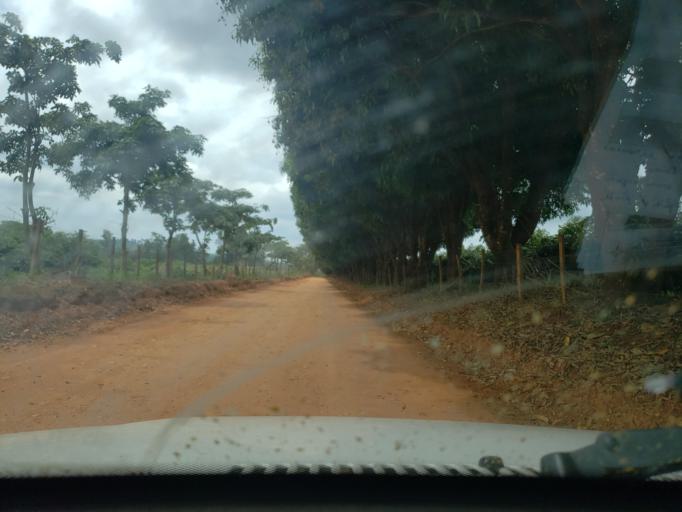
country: BR
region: Minas Gerais
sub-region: Boa Esperanca
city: Boa Esperanca
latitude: -20.9869
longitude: -45.5945
